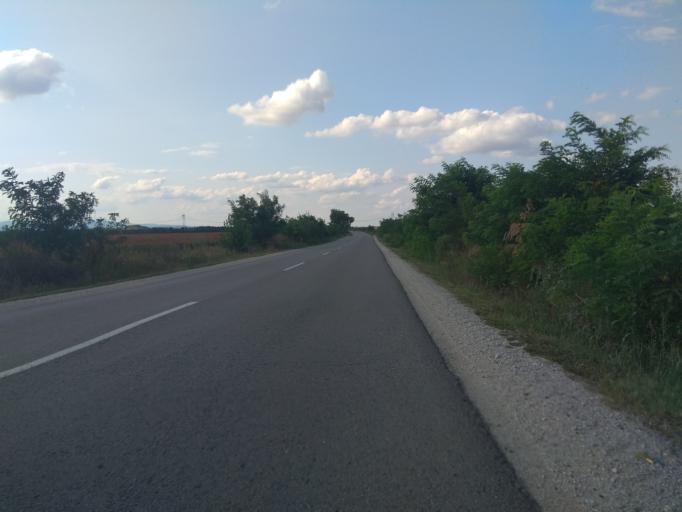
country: HU
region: Borsod-Abauj-Zemplen
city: Hejobaba
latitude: 47.9003
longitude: 20.8906
